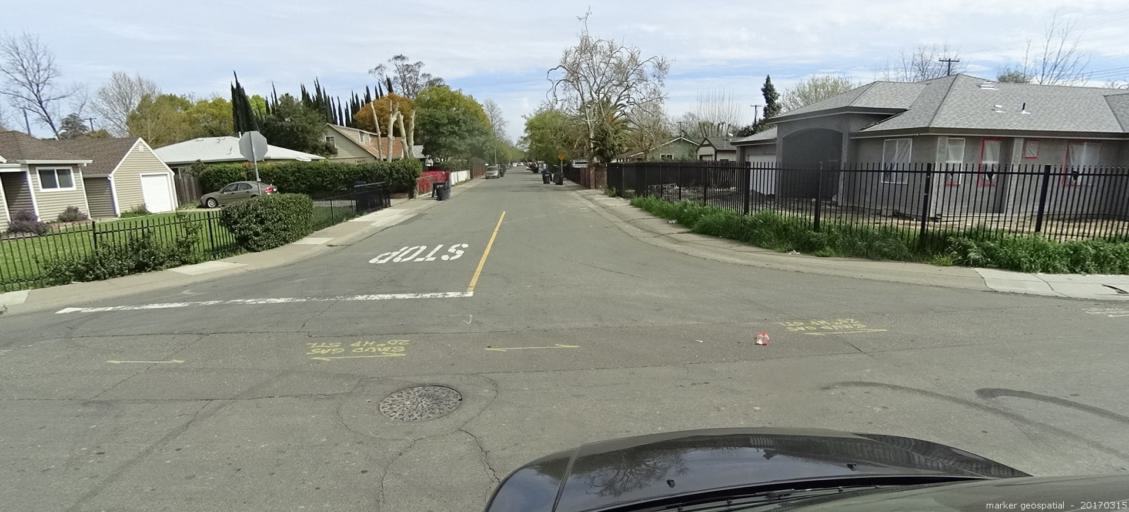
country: US
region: California
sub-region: Sacramento County
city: Parkway
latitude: 38.5224
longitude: -121.4773
